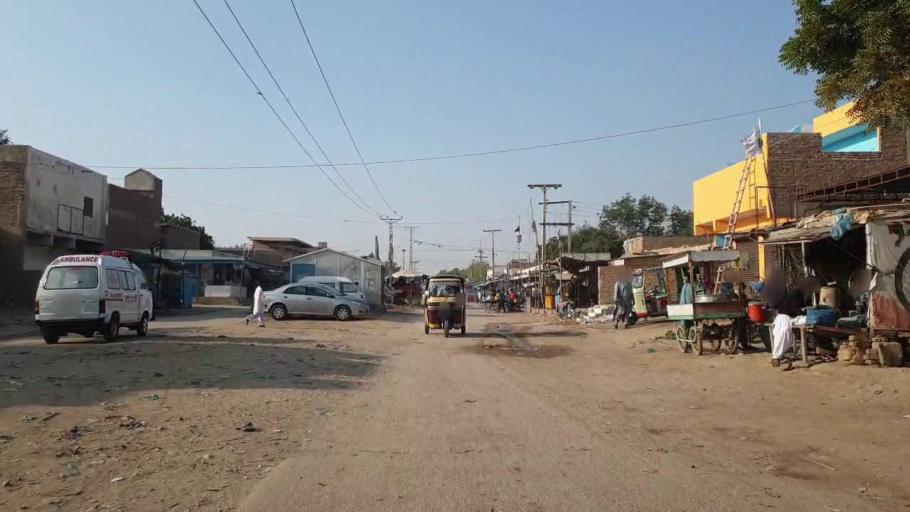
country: PK
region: Sindh
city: Kotri
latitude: 25.3570
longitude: 68.2562
